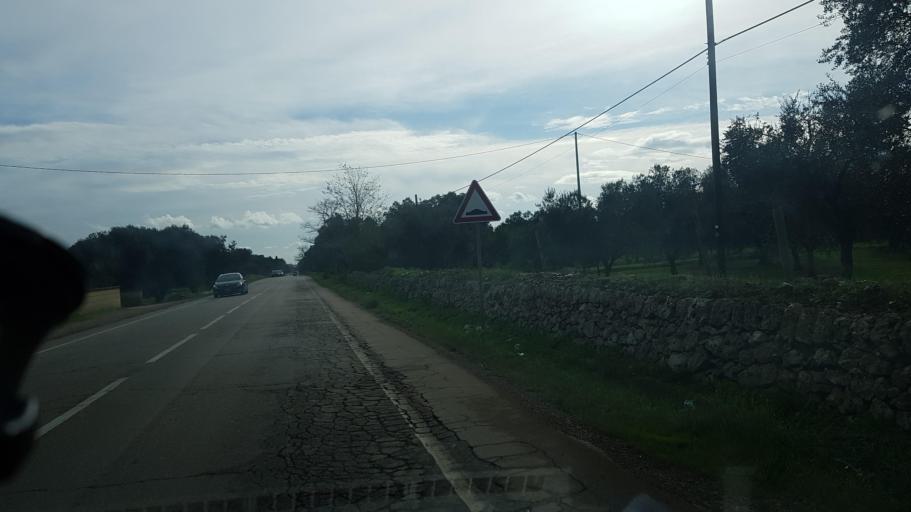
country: IT
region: Apulia
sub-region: Provincia di Brindisi
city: San Vito dei Normanni
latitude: 40.6753
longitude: 17.6893
